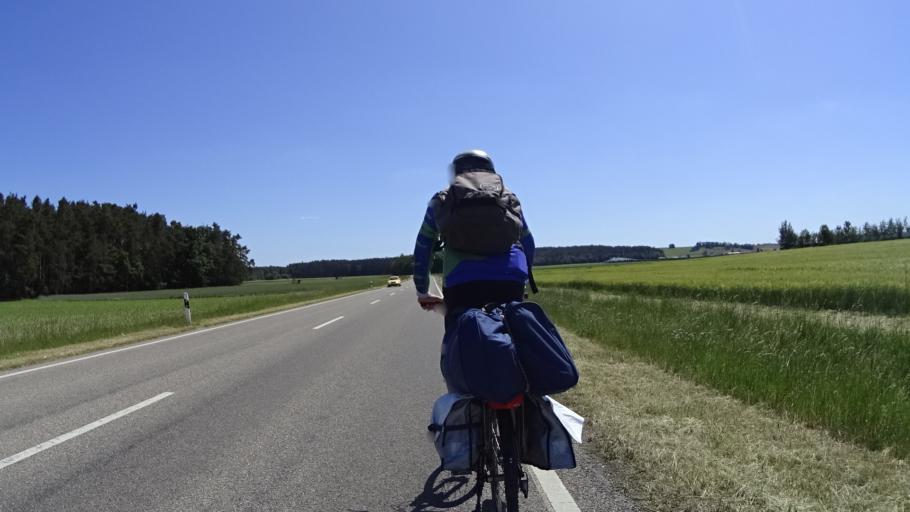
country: DE
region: Bavaria
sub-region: Regierungsbezirk Mittelfranken
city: Pfofeld
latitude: 49.1173
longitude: 10.8067
